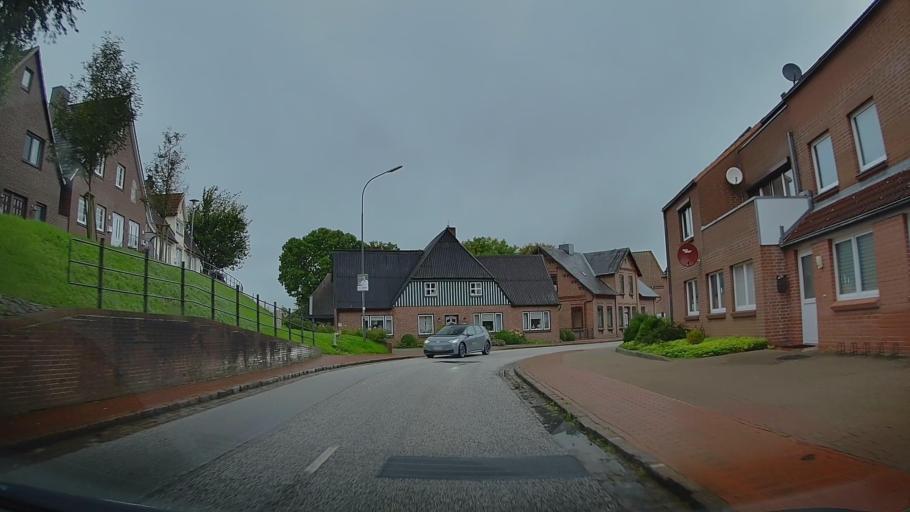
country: DE
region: Schleswig-Holstein
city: Sankt Margarethen
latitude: 53.8912
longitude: 9.2544
